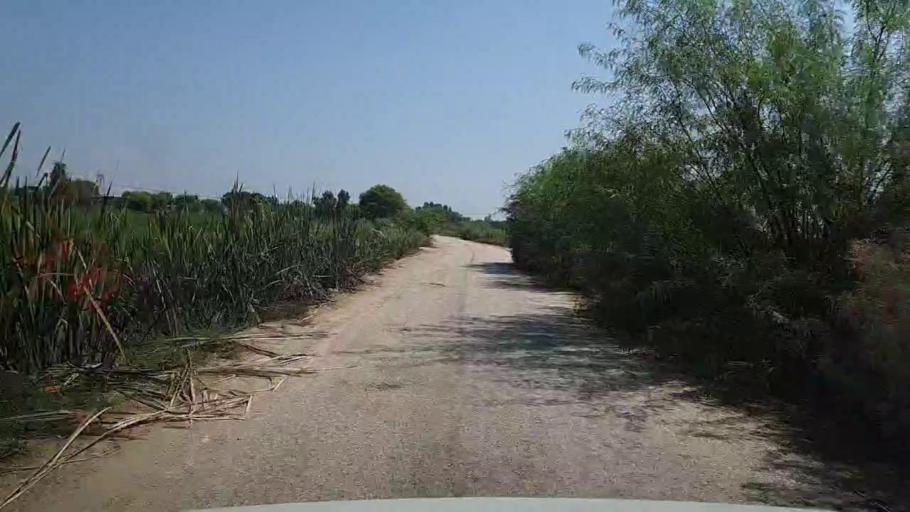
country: PK
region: Sindh
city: Kandhkot
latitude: 28.2912
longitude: 69.3517
